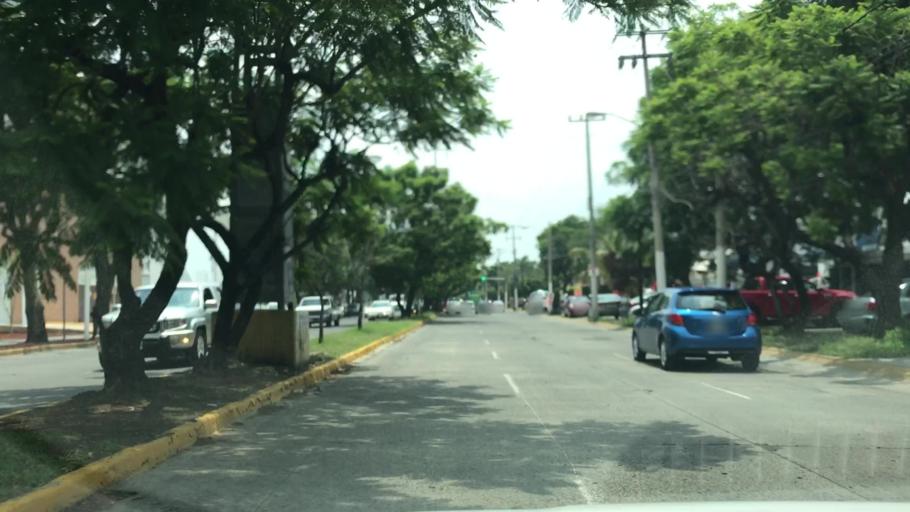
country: MX
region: Jalisco
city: Guadalajara
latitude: 20.6503
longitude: -103.4190
